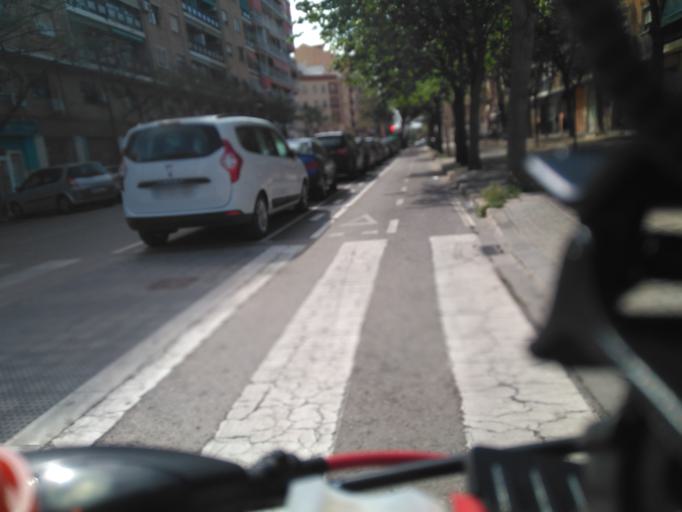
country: ES
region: Valencia
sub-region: Provincia de Valencia
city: Valencia
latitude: 39.4855
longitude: -0.3866
